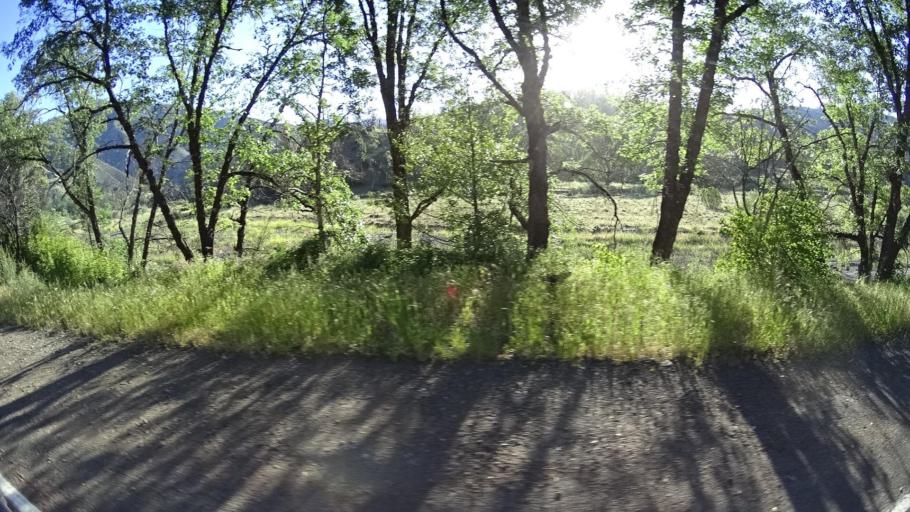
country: US
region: California
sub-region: Lake County
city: Upper Lake
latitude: 39.2480
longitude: -122.9517
